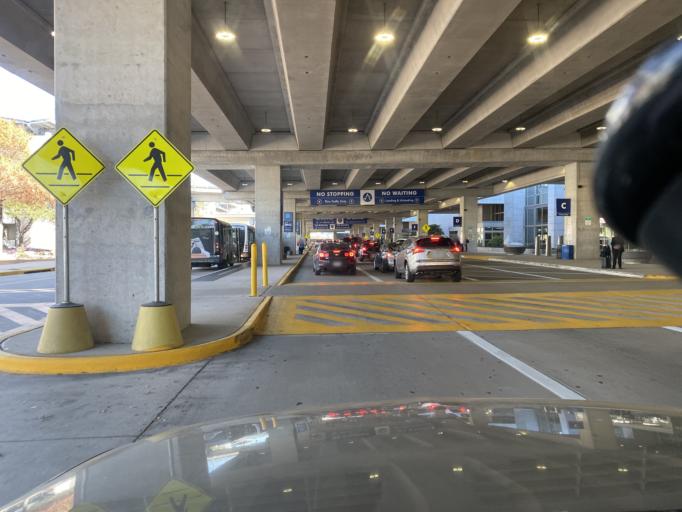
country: US
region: Texas
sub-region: Travis County
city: Hornsby Bend
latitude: 30.2027
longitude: -97.6686
